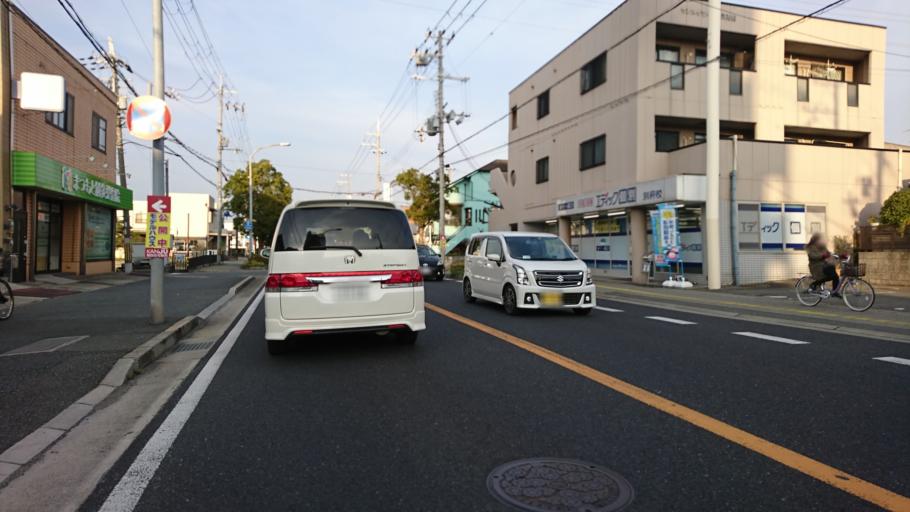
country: JP
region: Hyogo
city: Kakogawacho-honmachi
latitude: 34.7312
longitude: 134.8507
